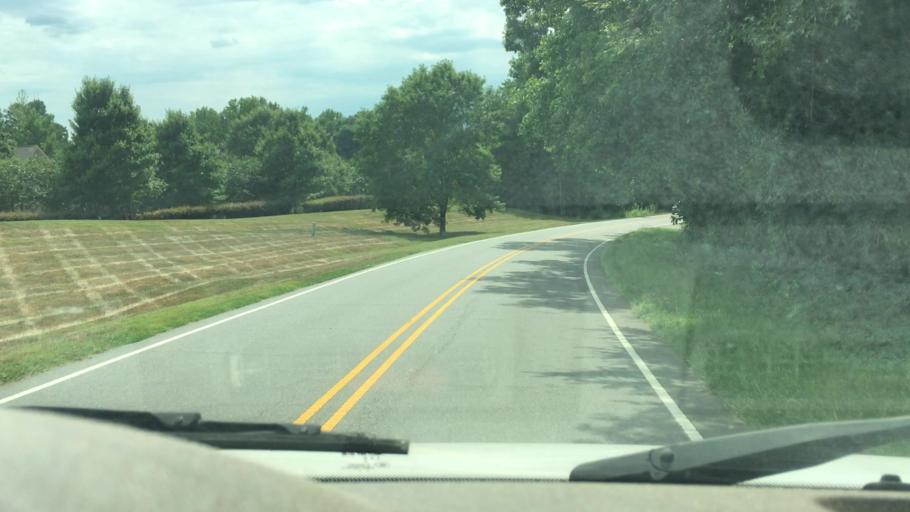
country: US
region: North Carolina
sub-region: Gaston County
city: Davidson
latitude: 35.4721
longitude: -80.7885
